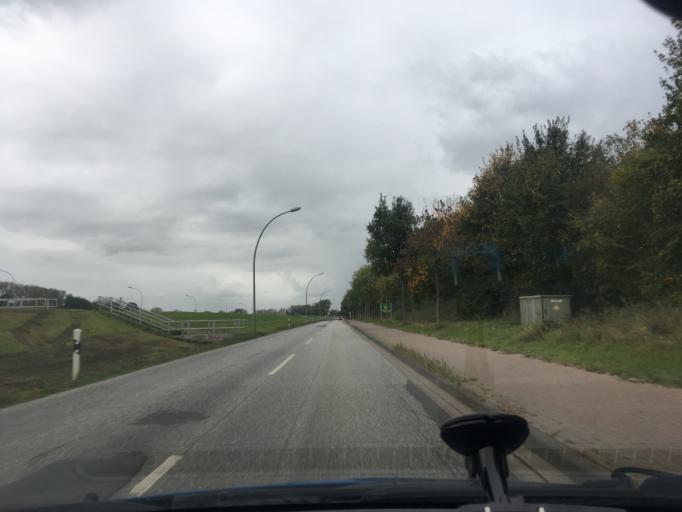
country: DE
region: Schleswig-Holstein
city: Escheburg
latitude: 53.4344
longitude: 10.3311
